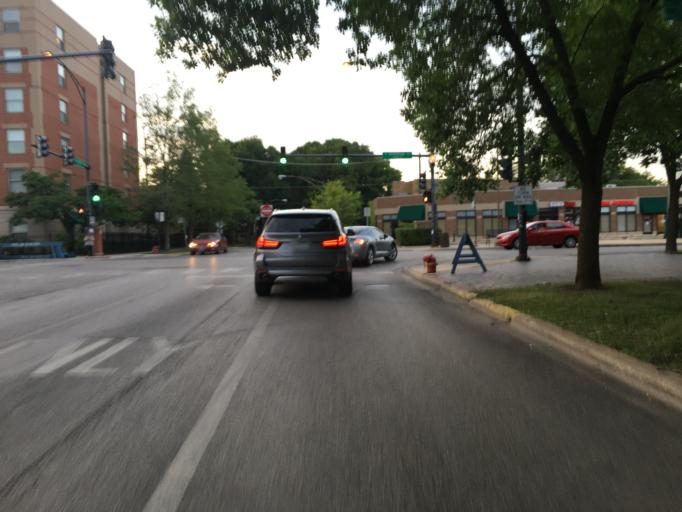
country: US
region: Illinois
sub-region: Cook County
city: Lincolnwood
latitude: 41.9610
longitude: -87.6985
